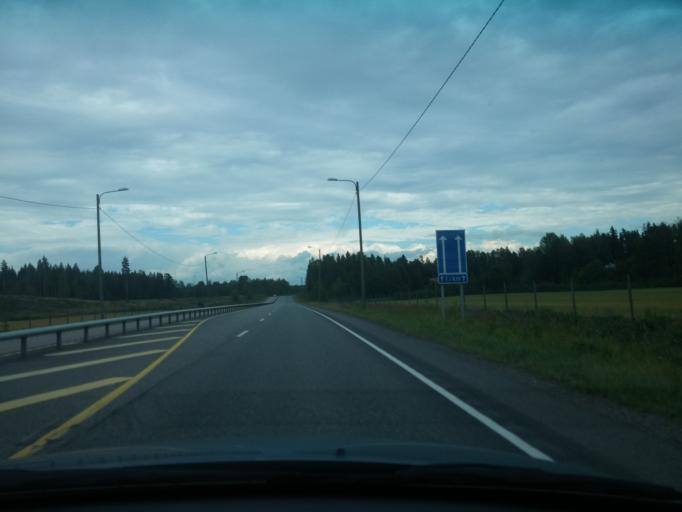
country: FI
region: Haeme
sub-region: Riihimaeki
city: Loppi
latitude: 60.7178
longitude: 24.4923
